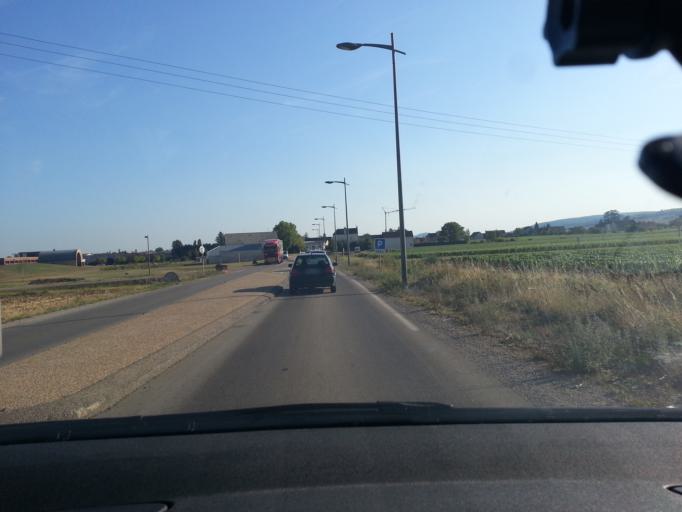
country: FR
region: Bourgogne
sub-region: Departement de la Cote-d'Or
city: Meursault
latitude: 46.9783
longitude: 4.7872
